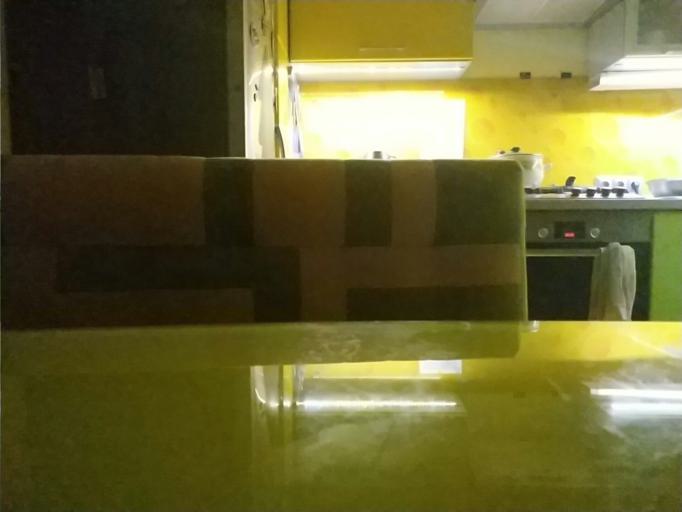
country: RU
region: Republic of Karelia
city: Pyaozerskiy
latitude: 65.5314
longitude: 30.5958
